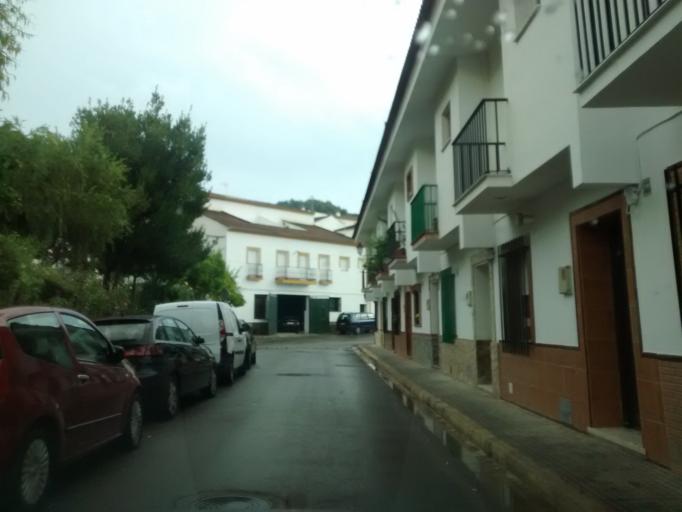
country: ES
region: Andalusia
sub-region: Provincia de Cadiz
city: El Bosque
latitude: 36.7575
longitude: -5.5040
